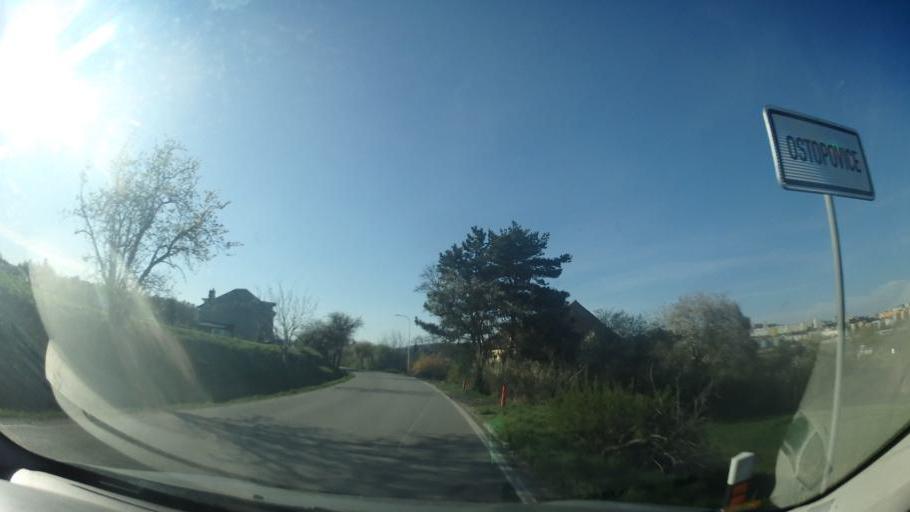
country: CZ
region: South Moravian
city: Ostopovice
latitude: 49.1584
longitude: 16.5519
